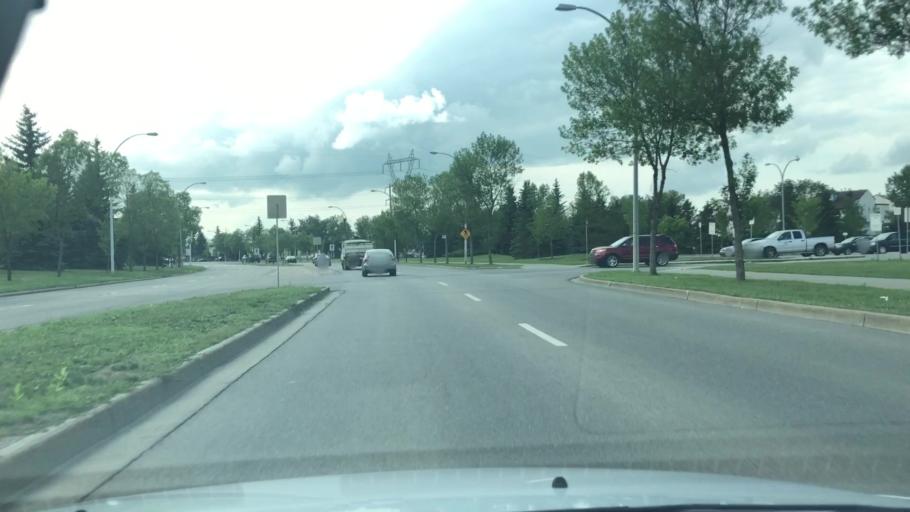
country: CA
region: Alberta
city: Edmonton
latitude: 53.6160
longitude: -113.5264
